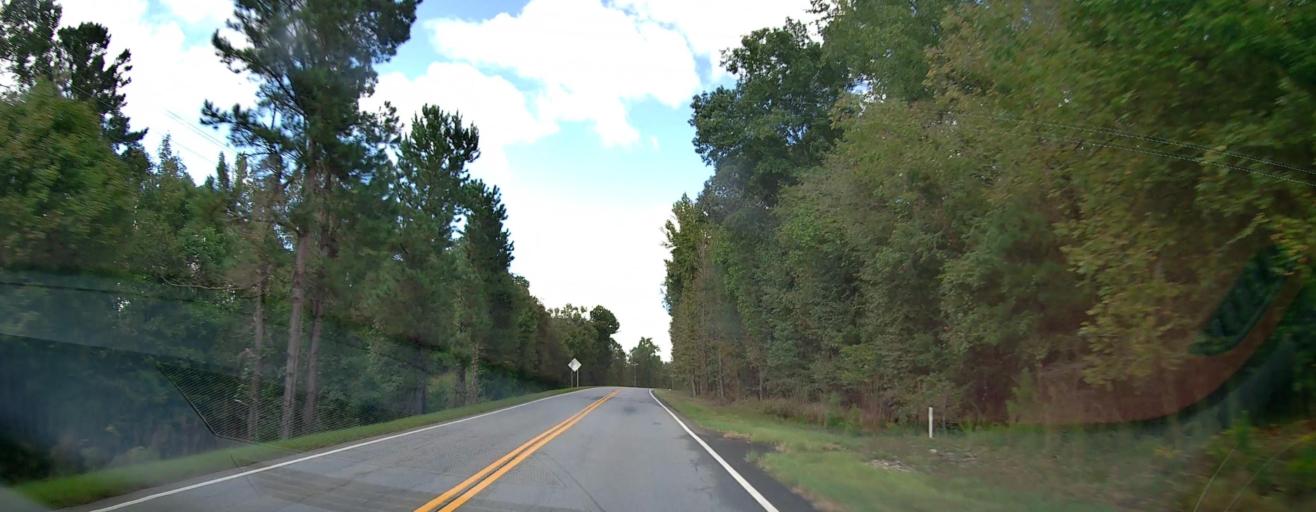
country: US
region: Georgia
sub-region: Jones County
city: Gray
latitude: 32.9787
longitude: -83.4199
